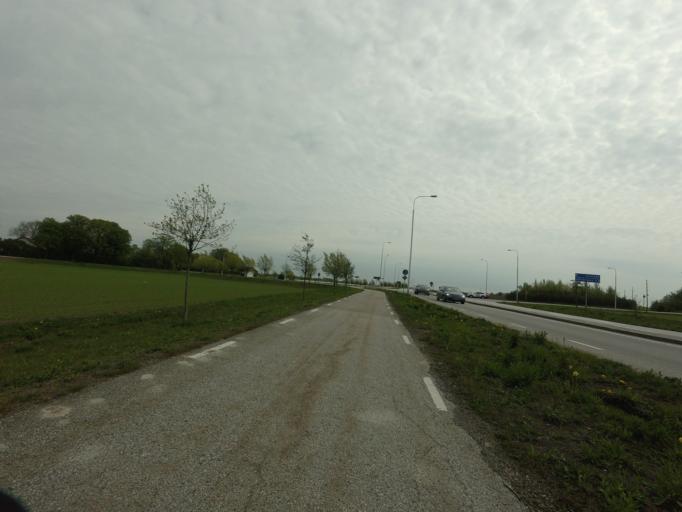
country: SE
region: Skane
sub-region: Malmo
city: Tygelsjo
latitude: 55.5420
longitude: 13.0373
